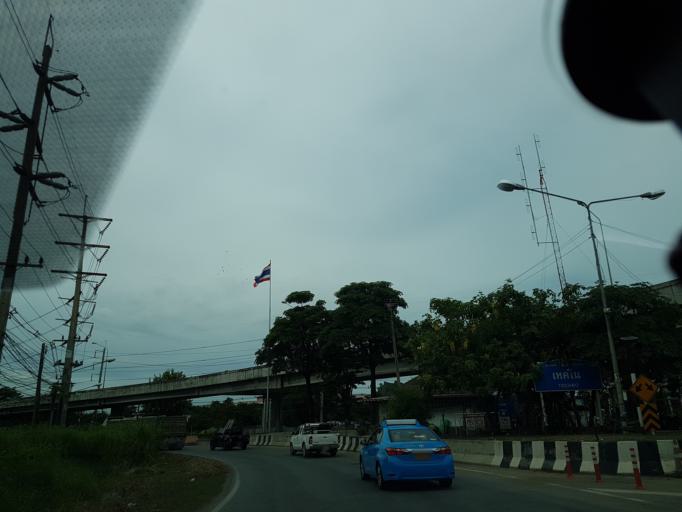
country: TH
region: Phra Nakhon Si Ayutthaya
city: Ban Bang Kadi Pathum Thani
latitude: 14.0153
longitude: 100.5506
